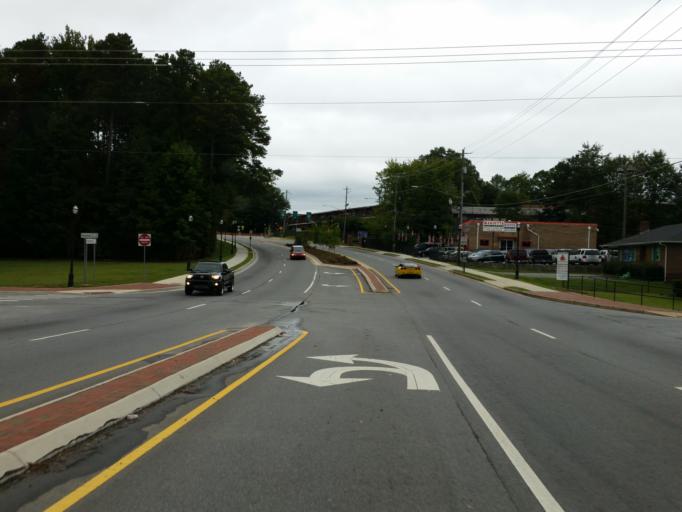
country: US
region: Georgia
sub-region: Cobb County
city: Marietta
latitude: 33.9646
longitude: -84.5369
